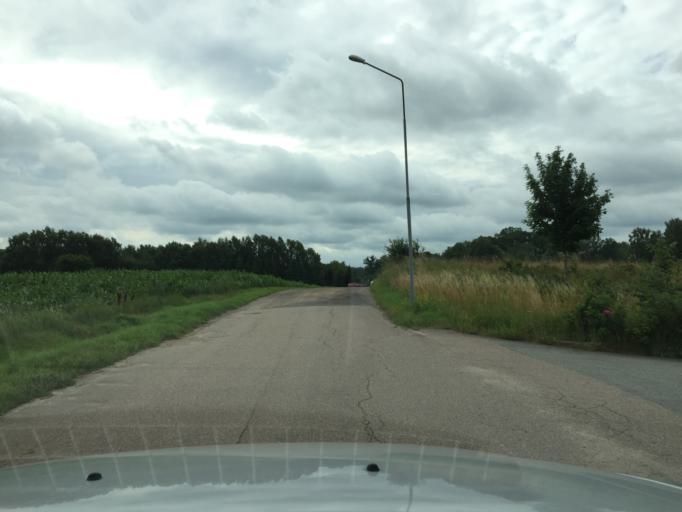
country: SE
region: Skane
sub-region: Hassleholms Kommun
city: Sosdala
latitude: 56.0375
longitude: 13.6902
